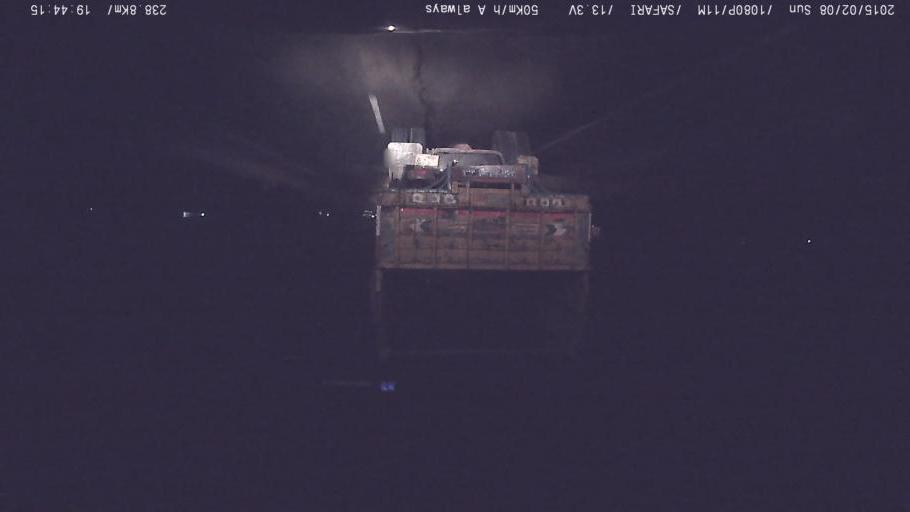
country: IN
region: Tamil Nadu
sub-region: Coimbatore
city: Irugur
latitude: 11.0439
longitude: 77.0780
